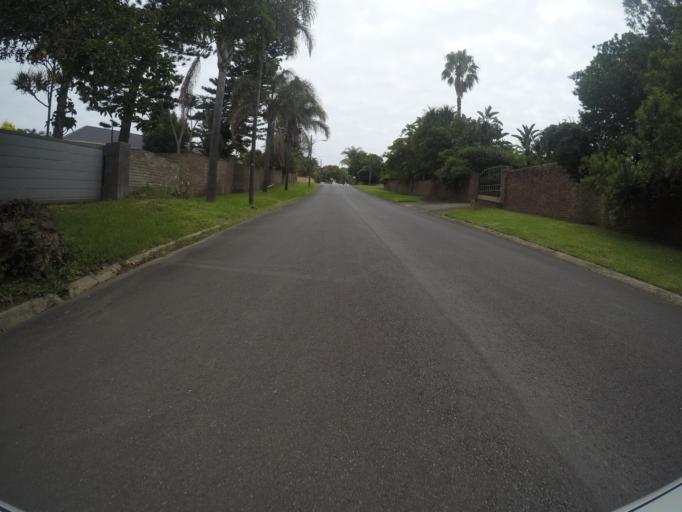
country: ZA
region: Eastern Cape
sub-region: Buffalo City Metropolitan Municipality
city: East London
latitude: -32.9740
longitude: 27.9430
